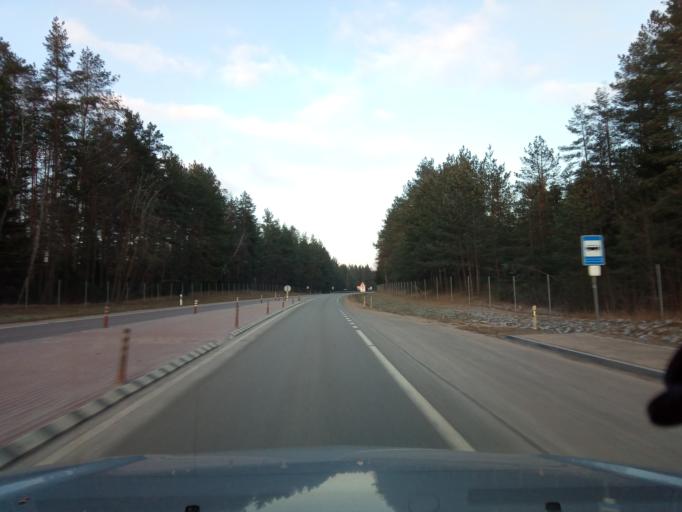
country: LT
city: Trakai
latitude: 54.5328
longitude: 24.9878
